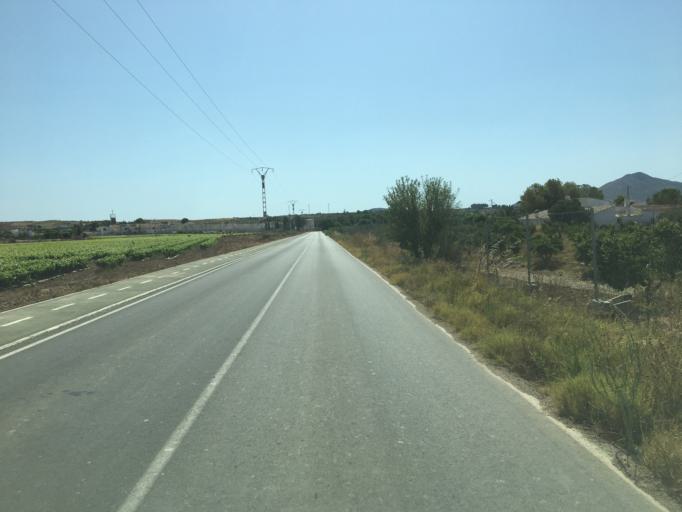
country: ES
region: Andalusia
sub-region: Provincia de Almeria
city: Huercal-Overa
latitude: 37.4223
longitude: -1.8860
